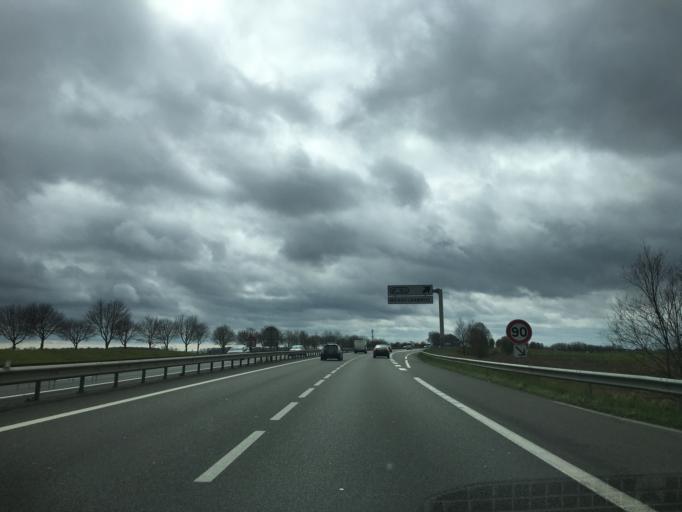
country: FR
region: Ile-de-France
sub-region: Departement de Seine-et-Marne
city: Moissy-Cramayel
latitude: 48.6381
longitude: 2.6281
